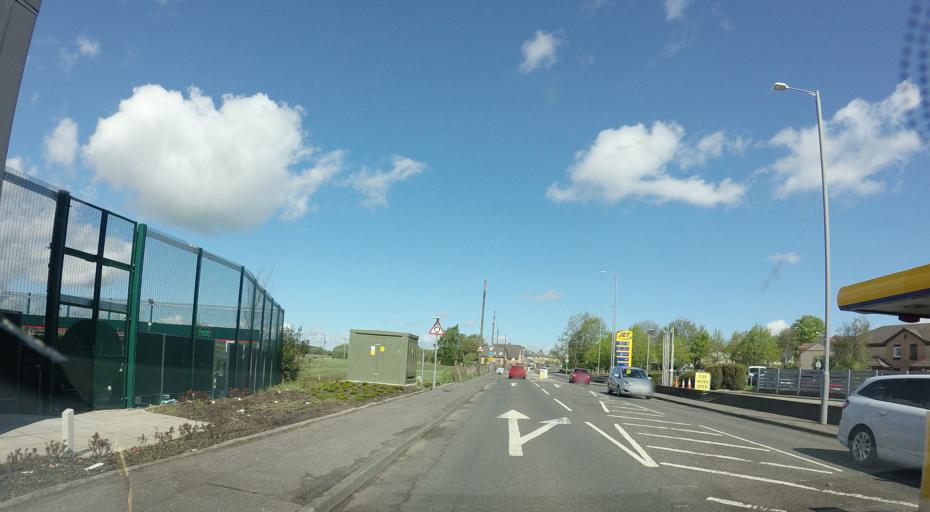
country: GB
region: Scotland
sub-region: Stirling
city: Bannockburn
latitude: 56.0876
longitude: -3.9299
